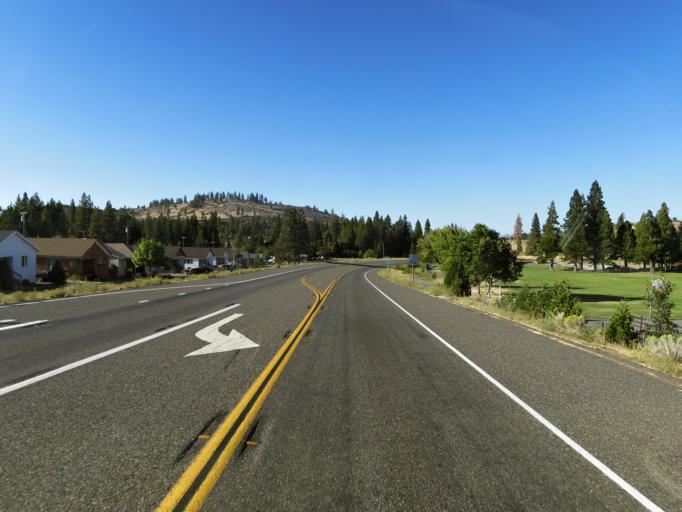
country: US
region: California
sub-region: Siskiyou County
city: Weed
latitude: 41.4368
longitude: -122.3872
